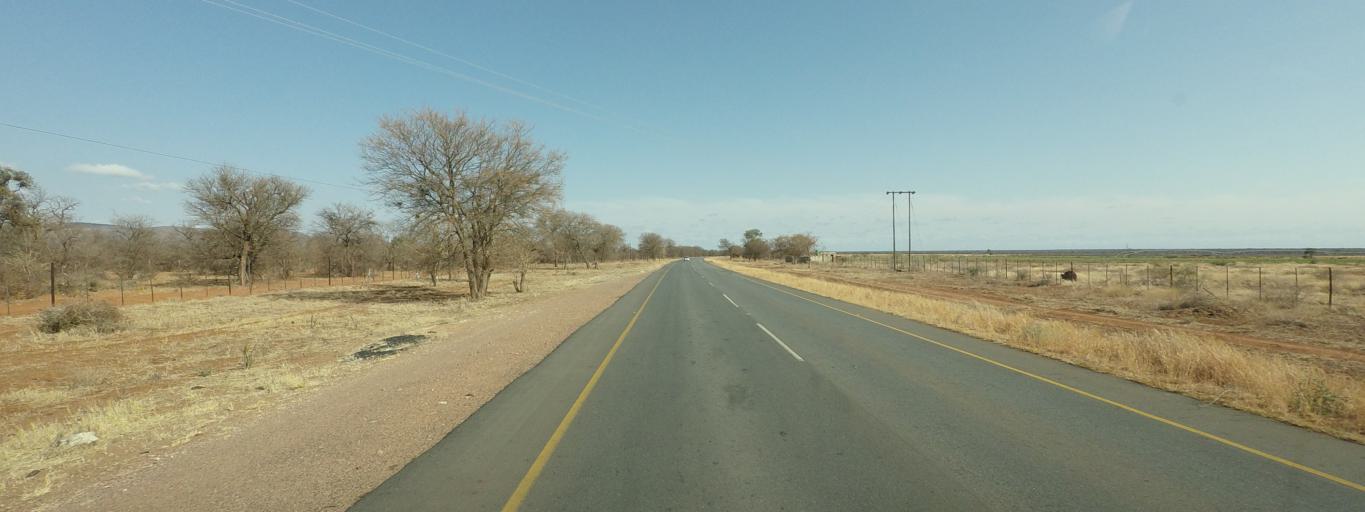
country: BW
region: Central
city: Makobeng
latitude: -22.9810
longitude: 27.9196
